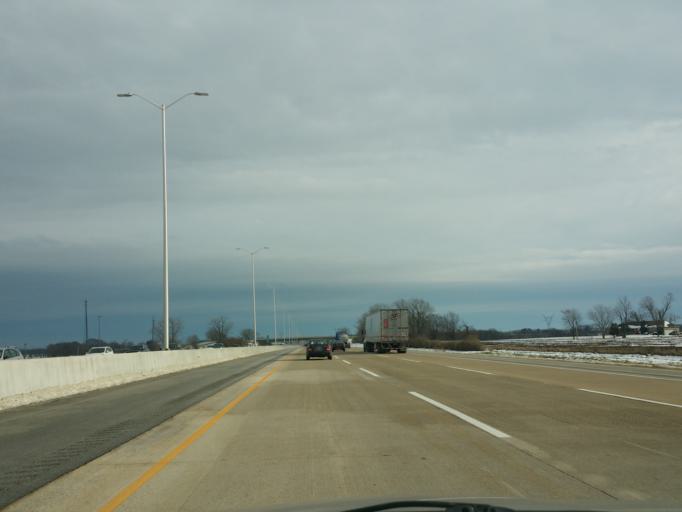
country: US
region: Illinois
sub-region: DeKalb County
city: Kingston
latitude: 42.2134
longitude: -88.7293
